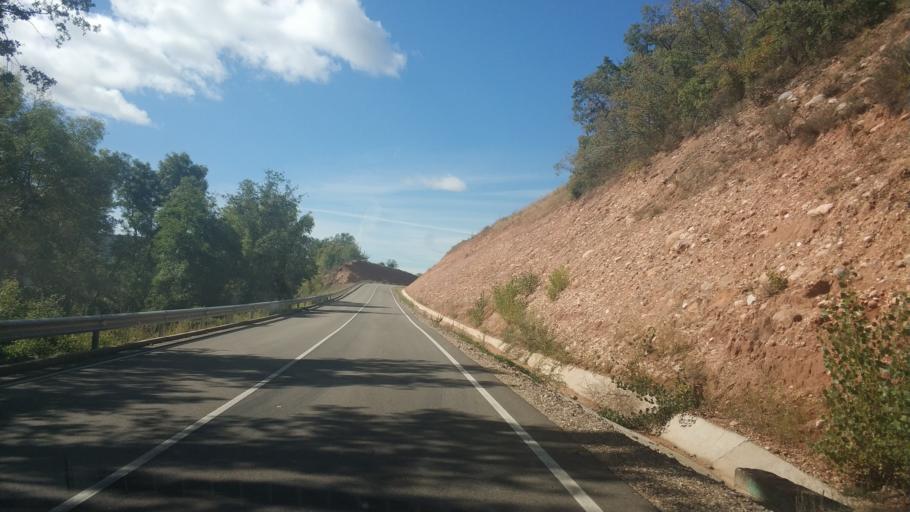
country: ES
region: Castille and Leon
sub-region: Provincia de Burgos
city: Covarrubias
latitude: 42.0476
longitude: -3.5433
